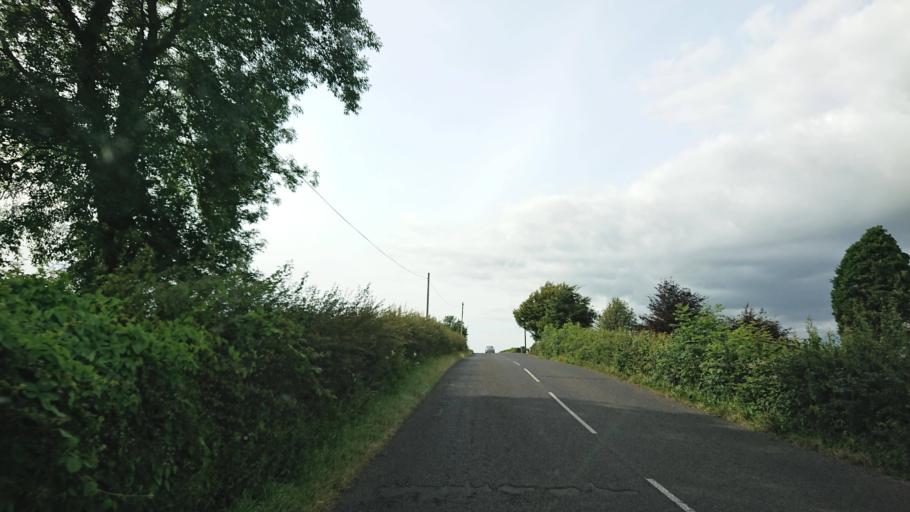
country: GB
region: Northern Ireland
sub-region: Fermanagh District
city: Enniskillen
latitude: 54.2866
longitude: -7.8645
